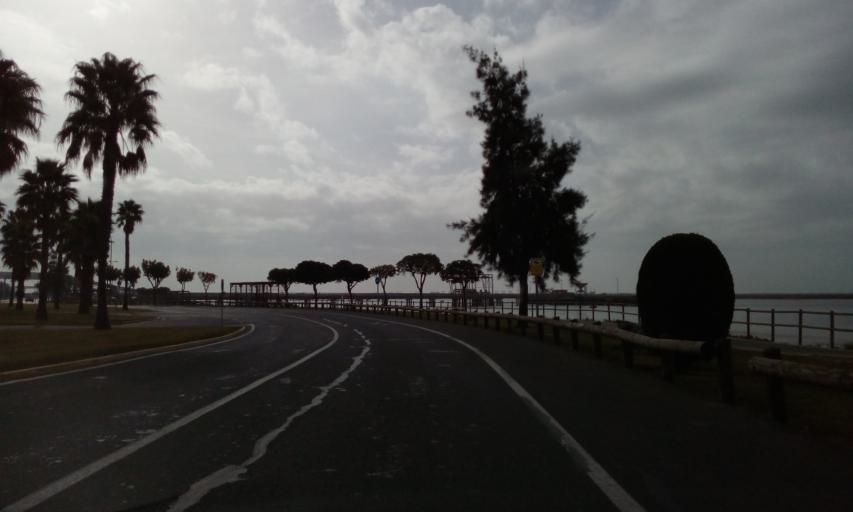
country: ES
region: Andalusia
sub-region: Provincia de Huelva
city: Huelva
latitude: 37.2329
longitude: -6.9533
